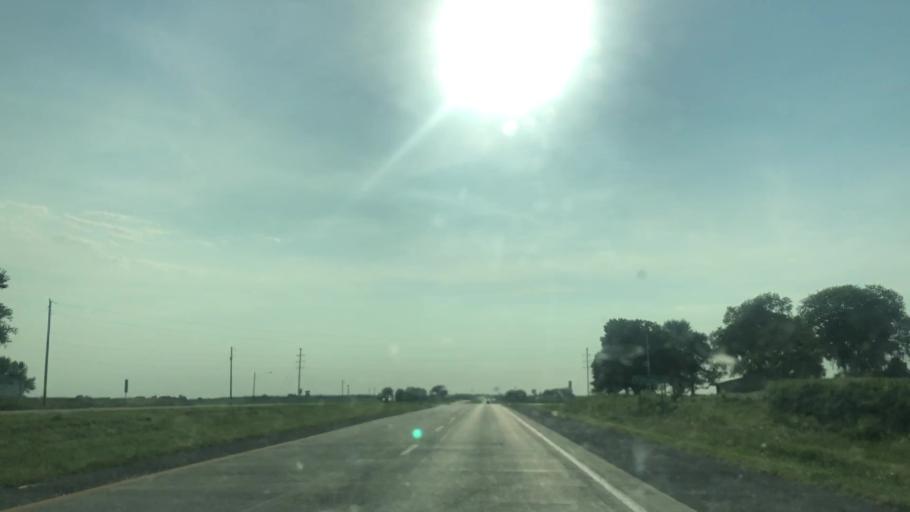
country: US
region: Iowa
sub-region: Story County
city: Nevada
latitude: 42.0080
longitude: -93.4032
